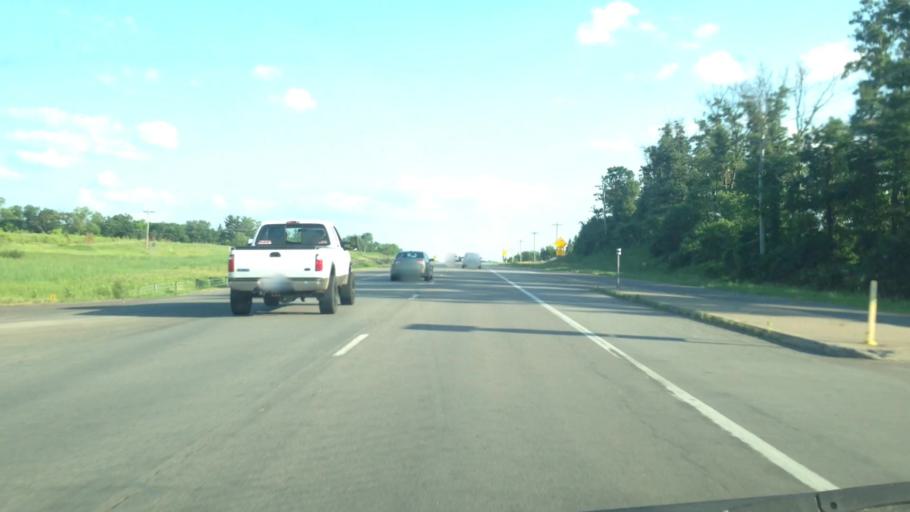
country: US
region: Minnesota
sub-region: Sherburne County
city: Zimmerman
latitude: 45.3786
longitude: -93.5644
